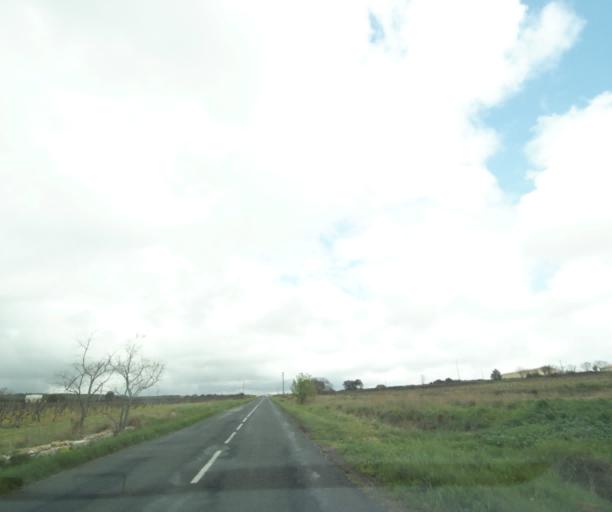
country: FR
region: Languedoc-Roussillon
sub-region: Departement de l'Herault
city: Cournonsec
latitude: 43.5346
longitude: 3.6973
